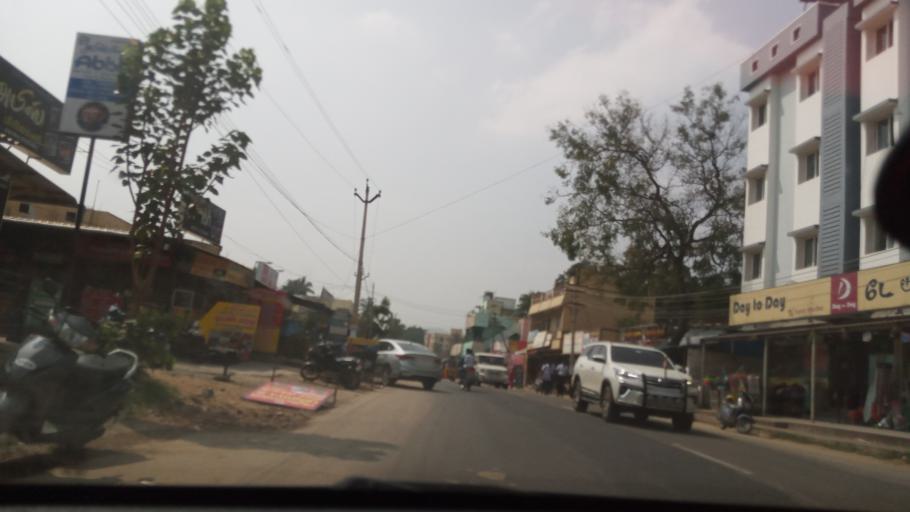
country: IN
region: Tamil Nadu
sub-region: Coimbatore
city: Perur
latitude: 11.0250
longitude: 76.9024
